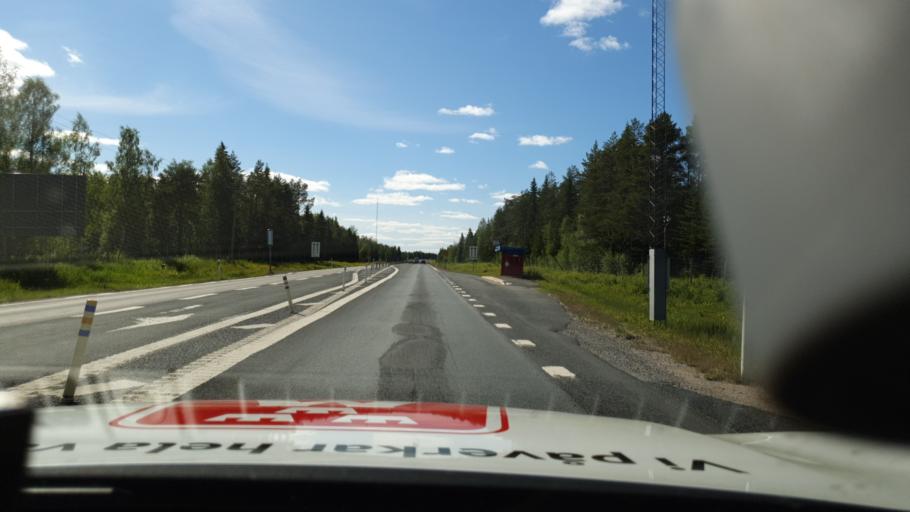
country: SE
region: Norrbotten
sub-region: Haparanda Kommun
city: Haparanda
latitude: 65.8116
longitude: 23.9121
